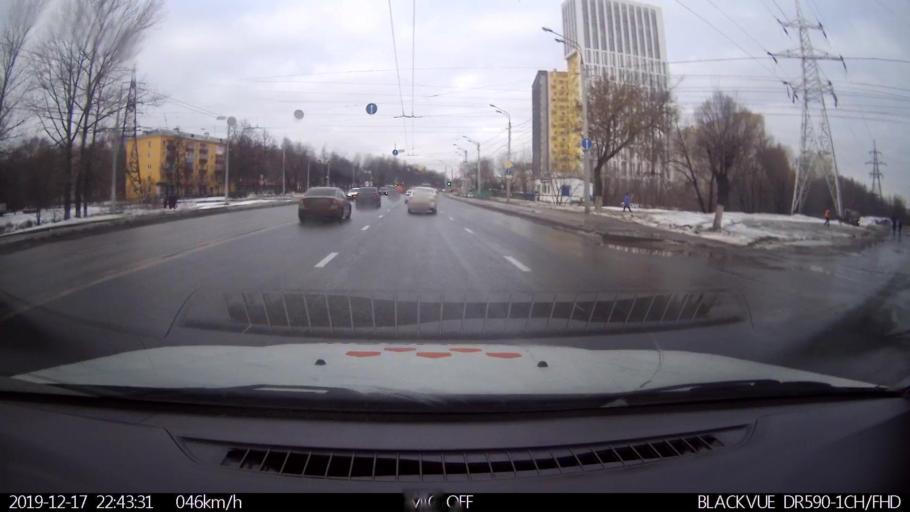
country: RU
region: Nizjnij Novgorod
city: Neklyudovo
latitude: 56.3440
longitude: 43.8744
